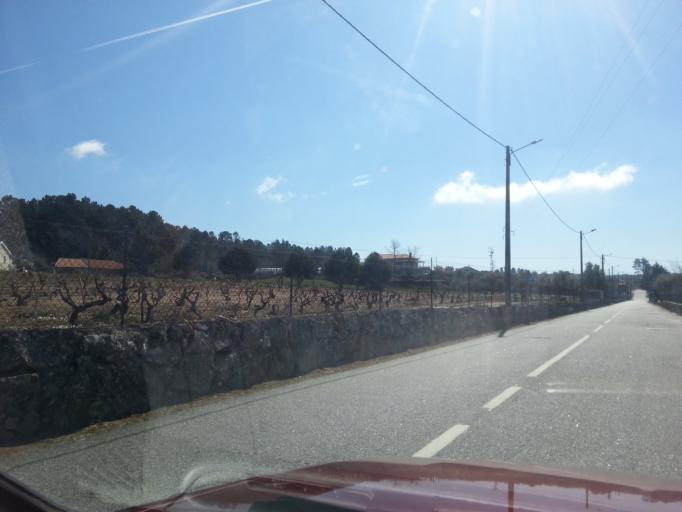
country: PT
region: Guarda
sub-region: Fornos de Algodres
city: Fornos de Algodres
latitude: 40.6503
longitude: -7.5344
